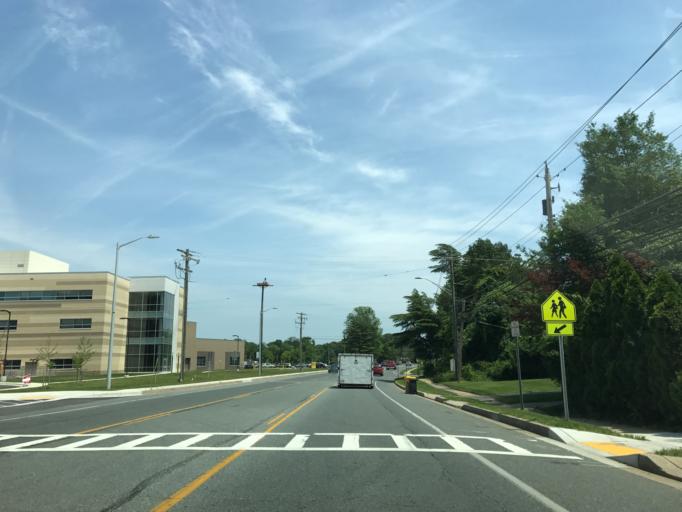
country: US
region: Maryland
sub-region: Anne Arundel County
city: Severna Park
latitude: 39.0762
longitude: -76.5625
